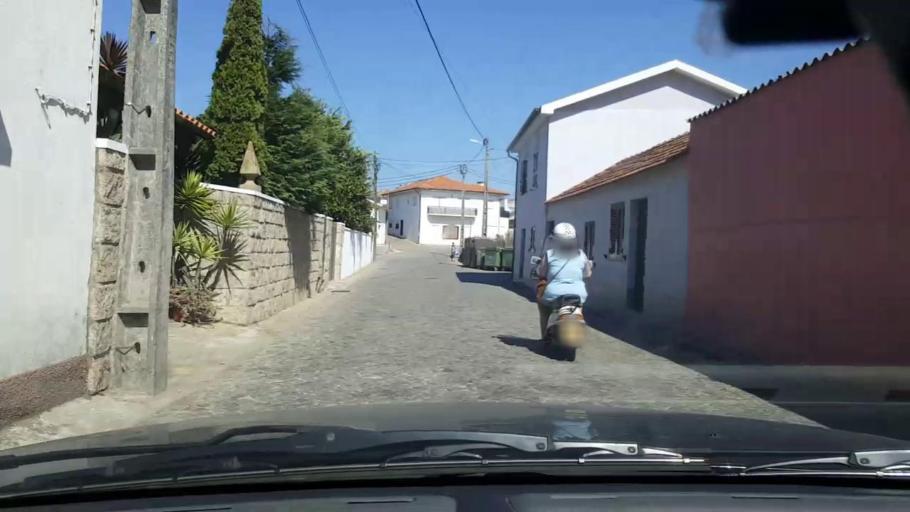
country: PT
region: Porto
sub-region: Matosinhos
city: Lavra
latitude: 41.2961
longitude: -8.7207
